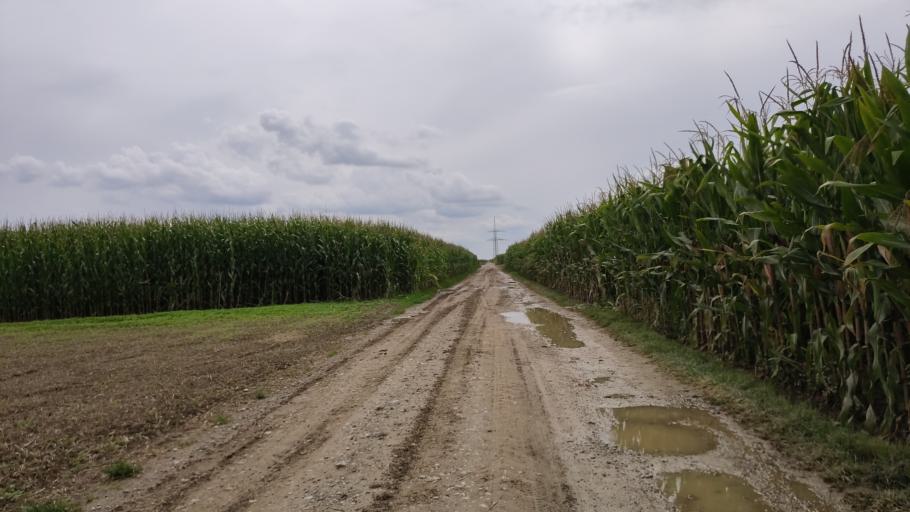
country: DE
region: Bavaria
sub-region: Swabia
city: Wehringen
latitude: 48.2408
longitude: 10.8224
